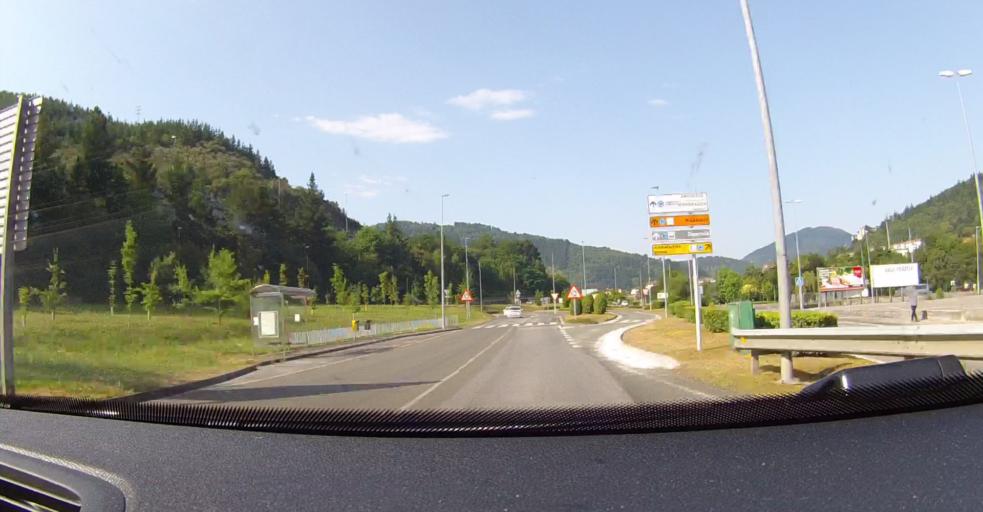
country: ES
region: Basque Country
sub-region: Provincia de Guipuzcoa
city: Arrasate / Mondragon
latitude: 43.0713
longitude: -2.4728
